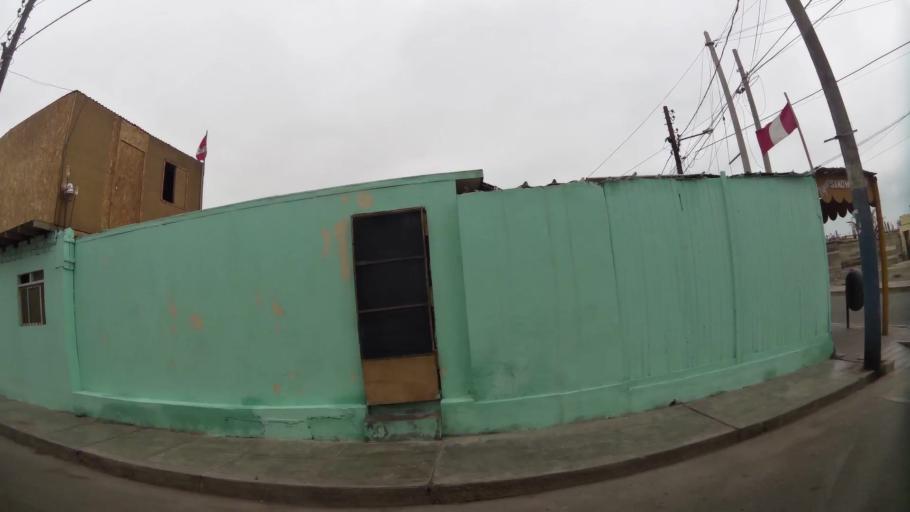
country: PE
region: Ica
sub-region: Provincia de Pisco
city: Pisco
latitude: -13.7085
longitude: -76.2177
